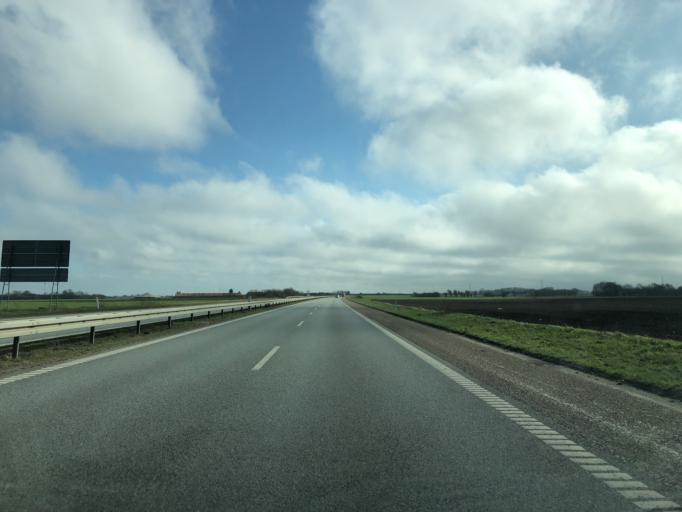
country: DK
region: North Denmark
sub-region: Hjorring Kommune
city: Hjorring
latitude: 57.4460
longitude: 10.0413
